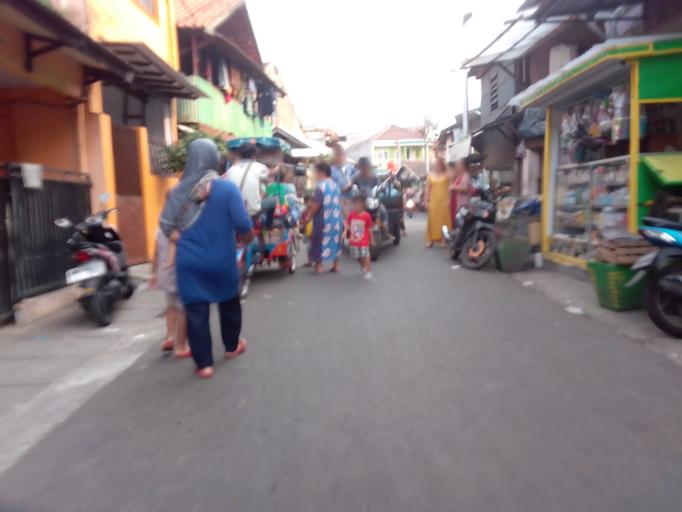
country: ID
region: Jakarta Raya
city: Jakarta
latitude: -6.1929
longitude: 106.8114
